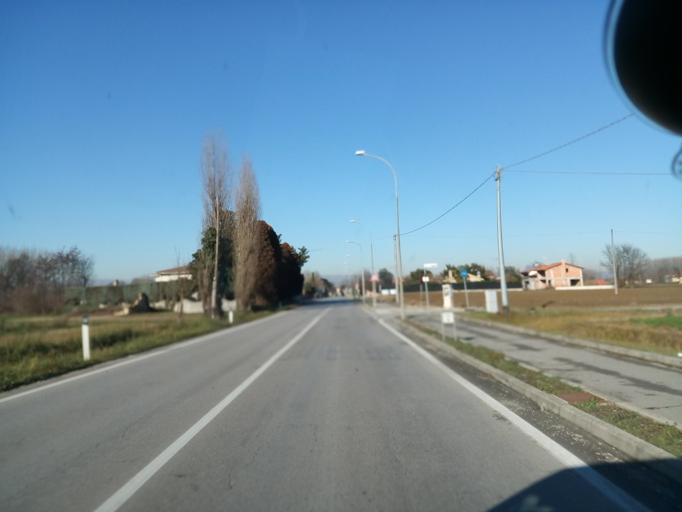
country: IT
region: Veneto
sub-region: Provincia di Padova
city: Massanzago-Ca' Baglioni-San Dono
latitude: 45.5814
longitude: 12.0038
